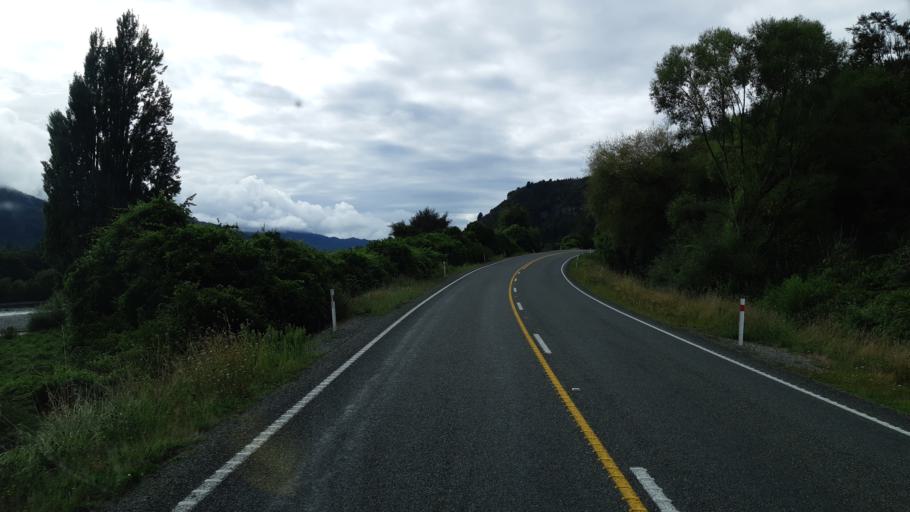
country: NZ
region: West Coast
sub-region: Buller District
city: Westport
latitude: -41.7798
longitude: 172.2564
